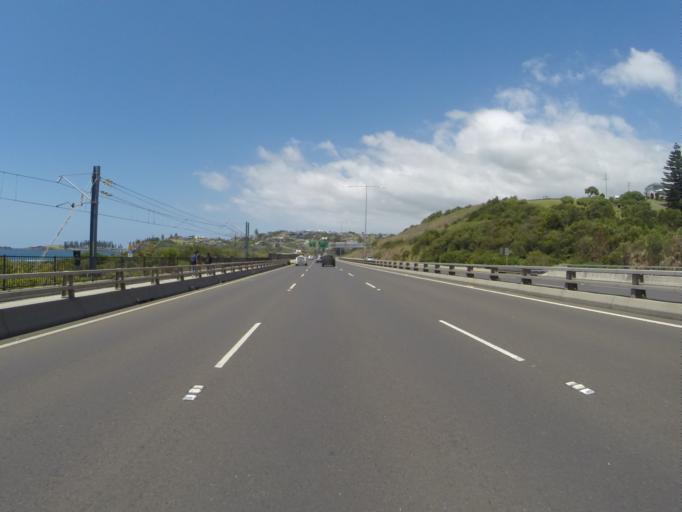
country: AU
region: New South Wales
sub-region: Kiama
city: Kiama
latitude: -34.6558
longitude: 150.8546
